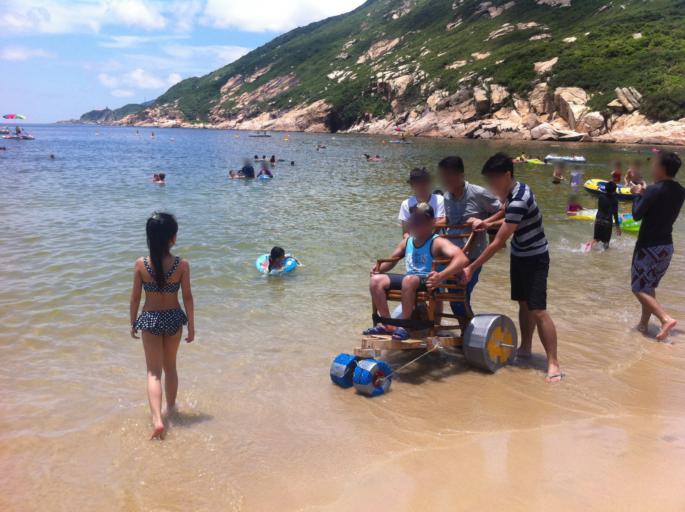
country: HK
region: Wanchai
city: Wan Chai
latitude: 22.2288
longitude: 114.2518
